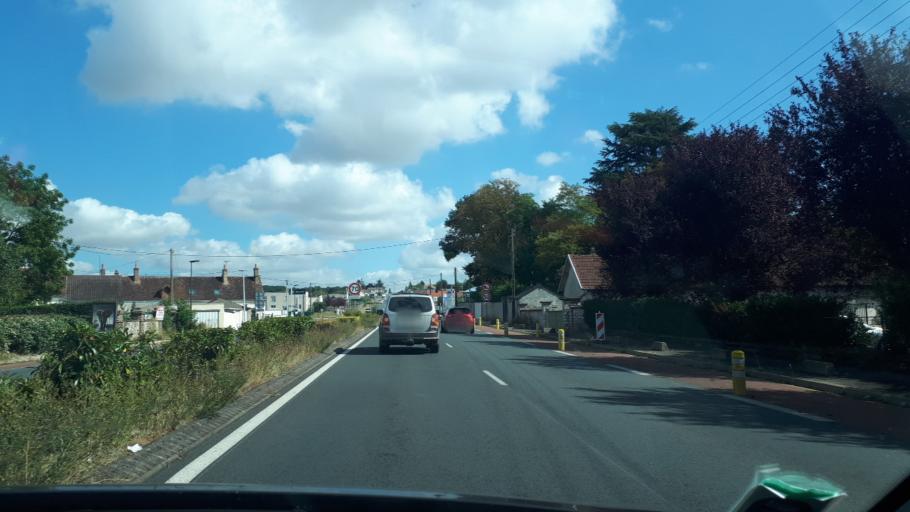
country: FR
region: Centre
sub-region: Departement du Loir-et-Cher
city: Vendome
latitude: 47.8070
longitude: 1.0723
